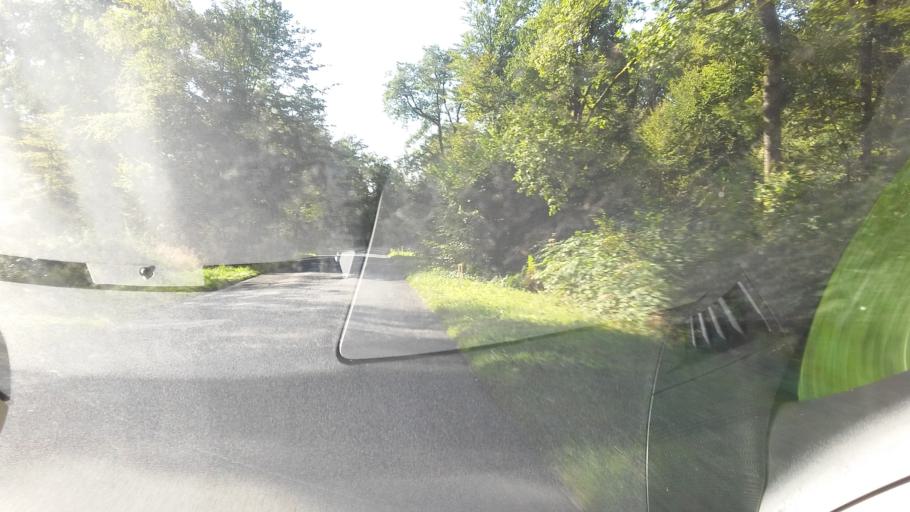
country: BE
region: Wallonia
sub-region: Province du Luxembourg
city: Neufchateau
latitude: 49.8025
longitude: 5.4151
